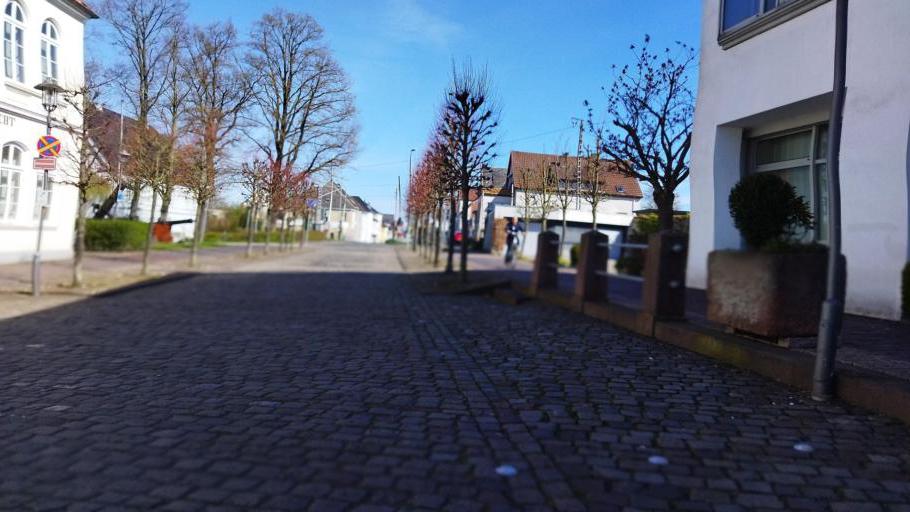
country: DE
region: Lower Saxony
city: Elsfleth
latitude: 53.2359
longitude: 8.4638
